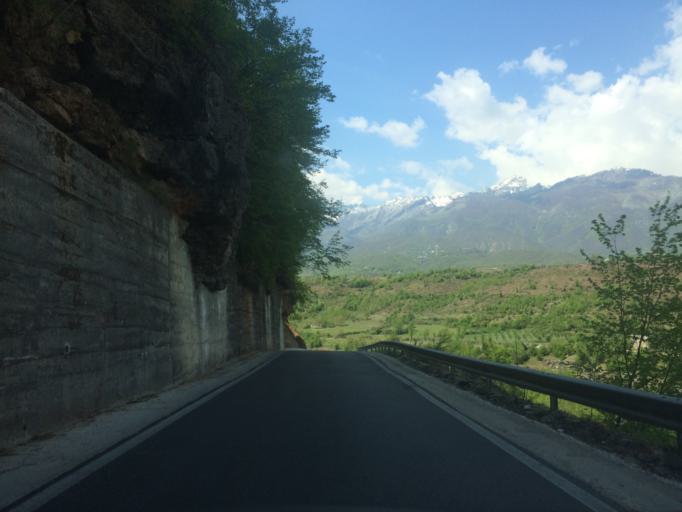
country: AL
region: Kukes
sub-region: Rrethi i Tropojes
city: Llugaj
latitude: 42.3535
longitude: 20.0968
